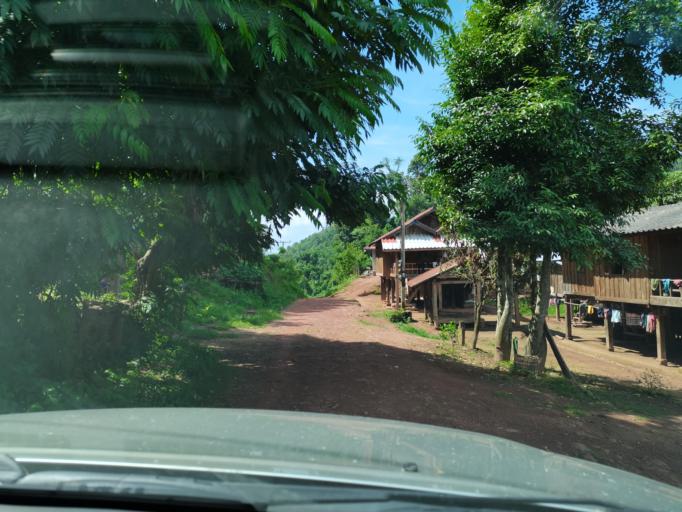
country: LA
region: Loungnamtha
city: Muang Nale
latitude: 20.5299
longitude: 101.0648
